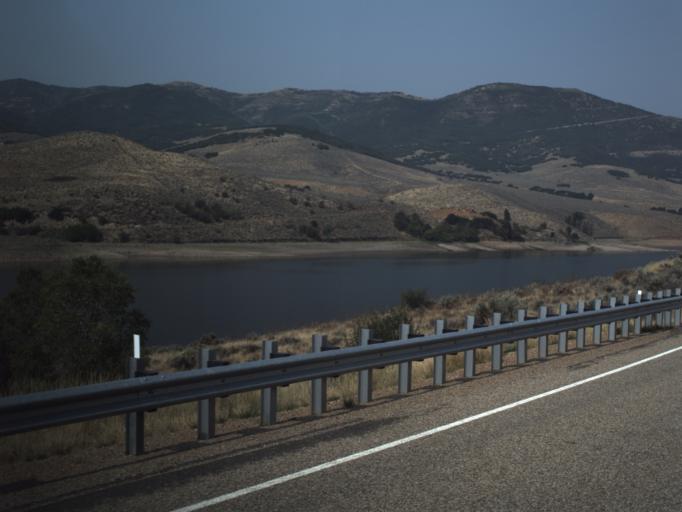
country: US
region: Utah
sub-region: Summit County
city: Summit Park
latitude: 40.8912
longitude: -111.5822
